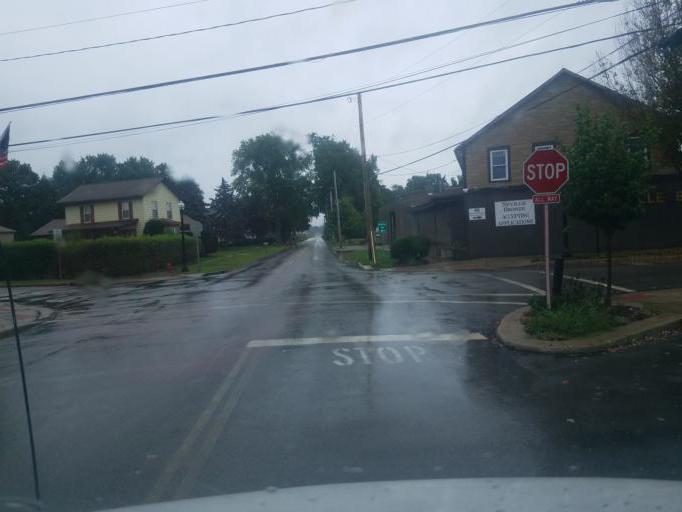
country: US
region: Ohio
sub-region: Medina County
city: Seville
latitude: 41.0093
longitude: -81.8619
